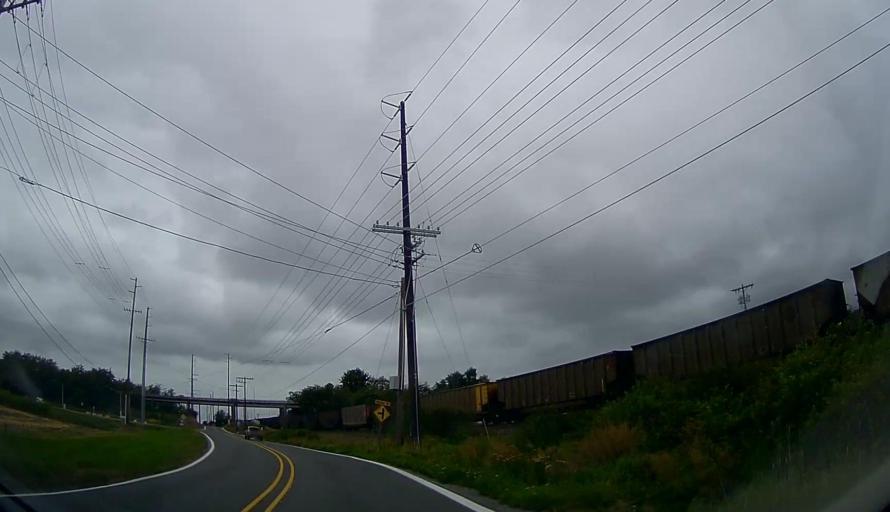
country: US
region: Washington
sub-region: Snohomish County
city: Stanwood
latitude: 48.2385
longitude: -122.3467
